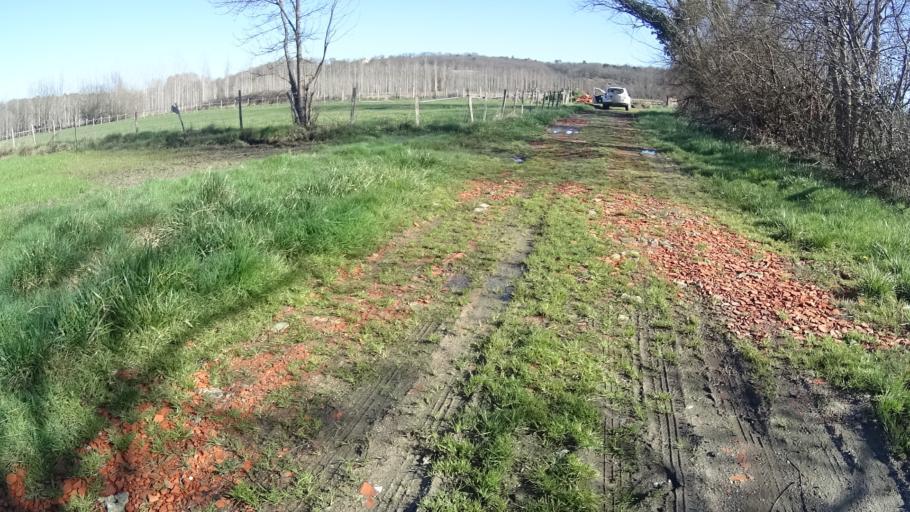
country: FR
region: Aquitaine
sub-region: Departement de la Dordogne
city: Saint-Aulaye
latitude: 45.2241
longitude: 0.0917
